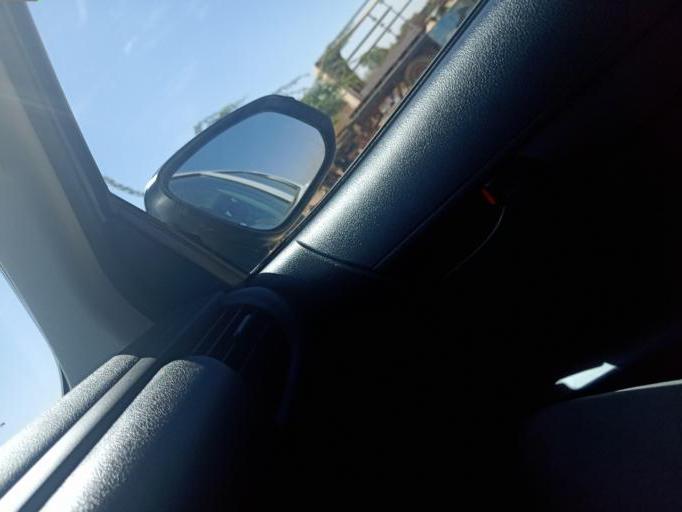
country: BF
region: Centre
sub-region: Kadiogo Province
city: Ouagadougou
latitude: 12.2920
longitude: -1.4665
